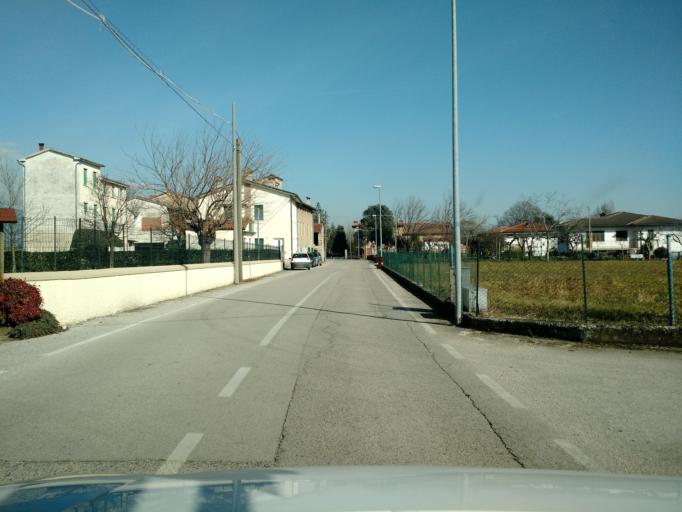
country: IT
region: Veneto
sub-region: Provincia di Vicenza
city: Marano Vicentino
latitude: 45.6849
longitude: 11.4550
